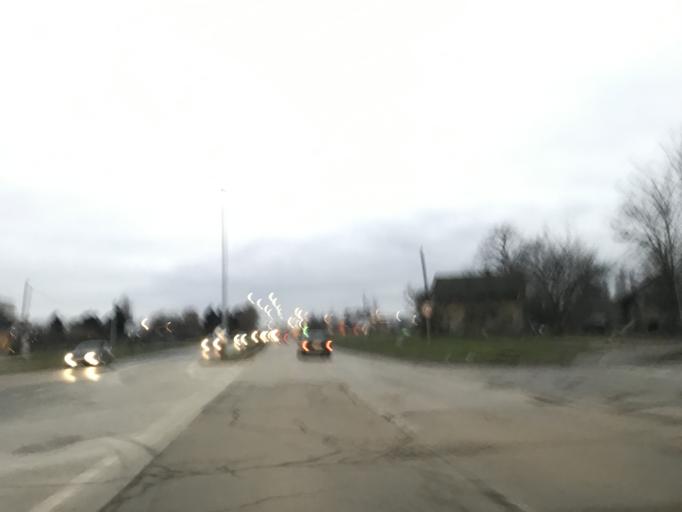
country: RS
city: Veternik
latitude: 45.2778
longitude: 19.7957
